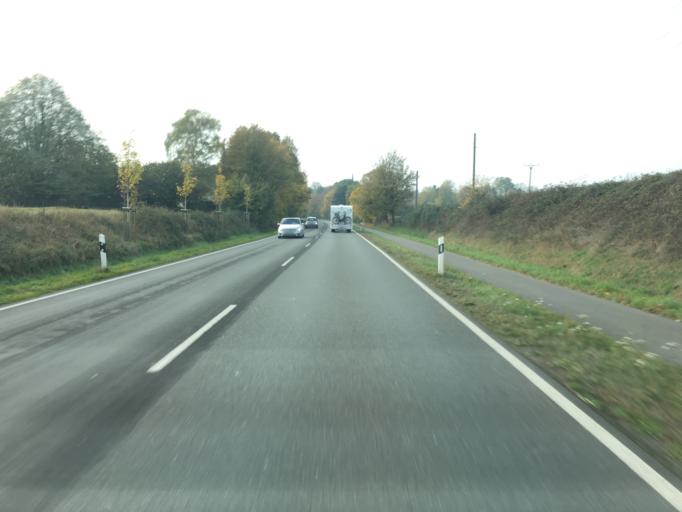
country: DE
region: North Rhine-Westphalia
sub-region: Regierungsbezirk Dusseldorf
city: Sonsbeck
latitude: 51.6194
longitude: 6.3841
